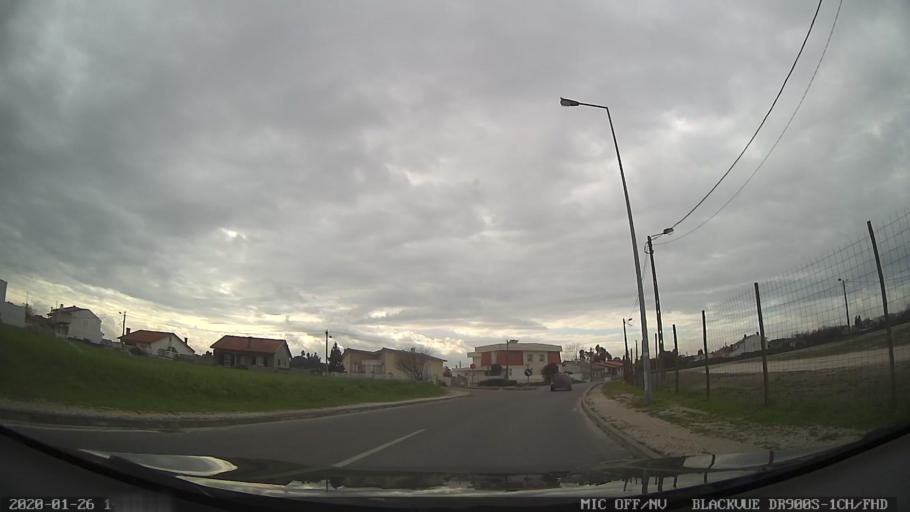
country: PT
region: Aveiro
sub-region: Aveiro
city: Aradas
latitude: 40.6313
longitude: -8.6301
